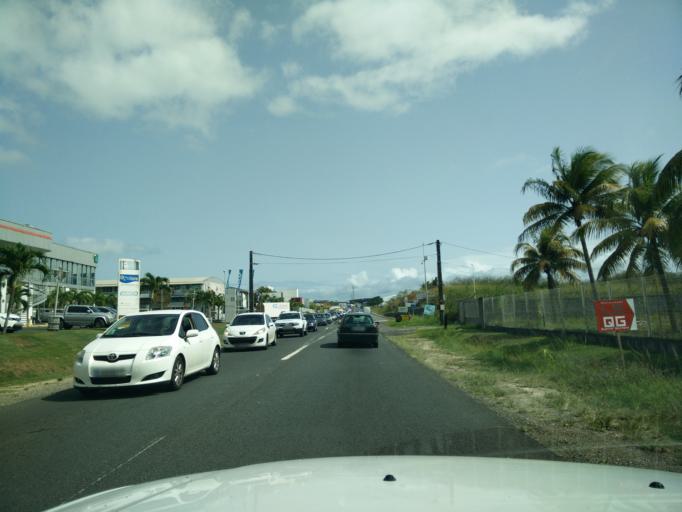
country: GP
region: Guadeloupe
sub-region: Guadeloupe
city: Baie-Mahault
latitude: 16.2484
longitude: -61.5712
